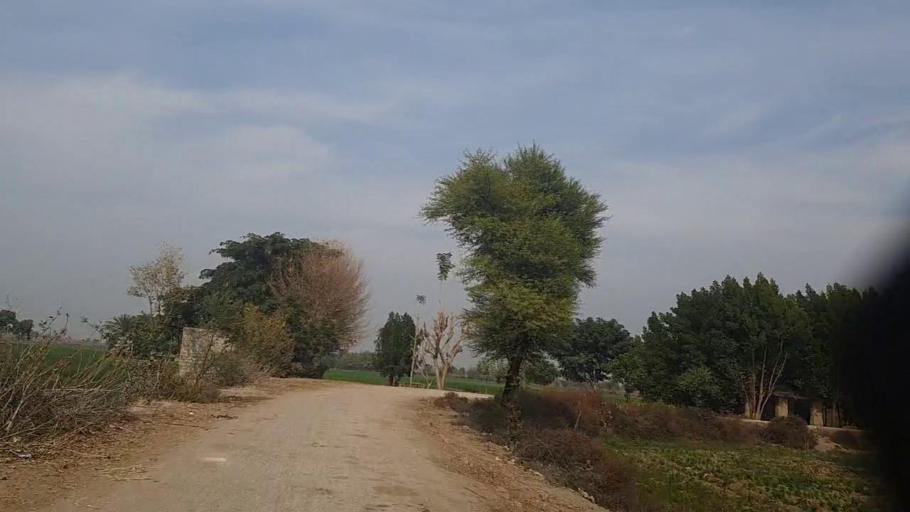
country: PK
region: Sindh
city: Daur
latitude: 26.3674
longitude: 68.2332
